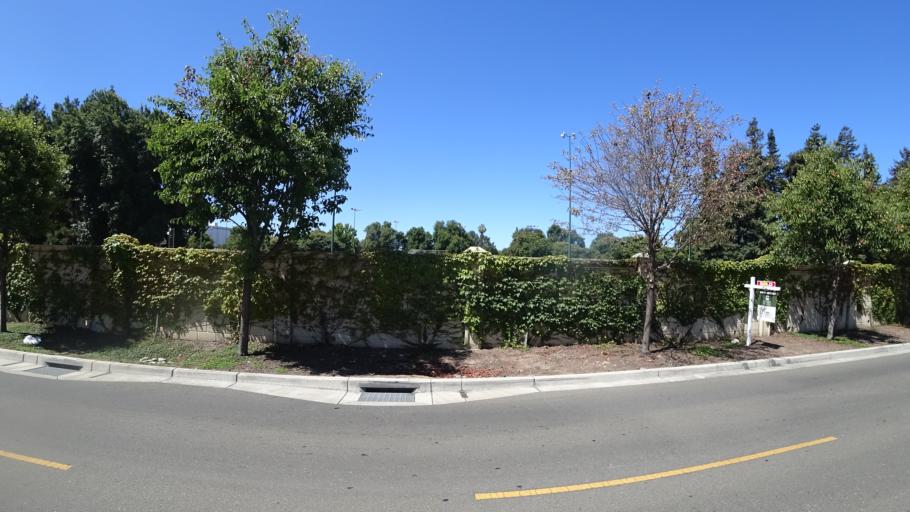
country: US
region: California
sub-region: Alameda County
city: Hayward
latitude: 37.6631
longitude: -122.0958
